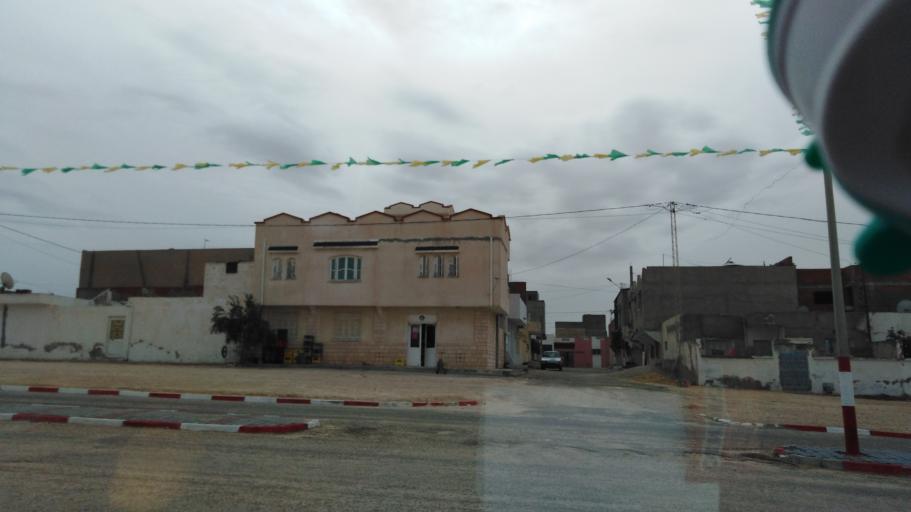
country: TN
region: Qabis
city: Gabes
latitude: 33.9499
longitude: 10.0030
